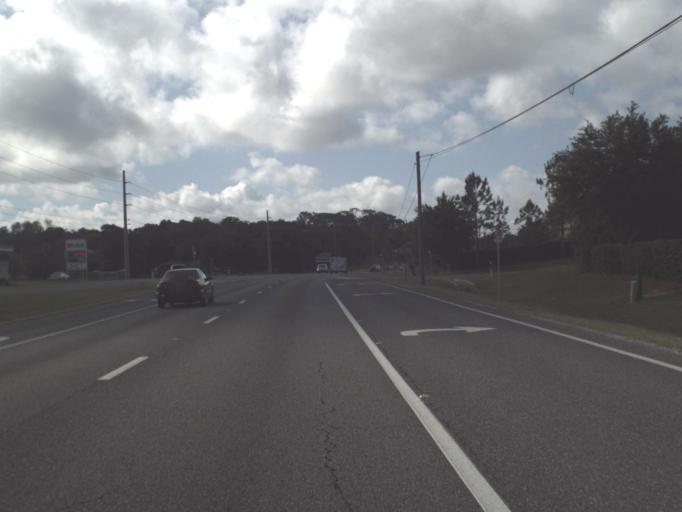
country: US
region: Florida
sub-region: Lake County
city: Lady Lake
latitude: 28.9006
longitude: -81.9125
